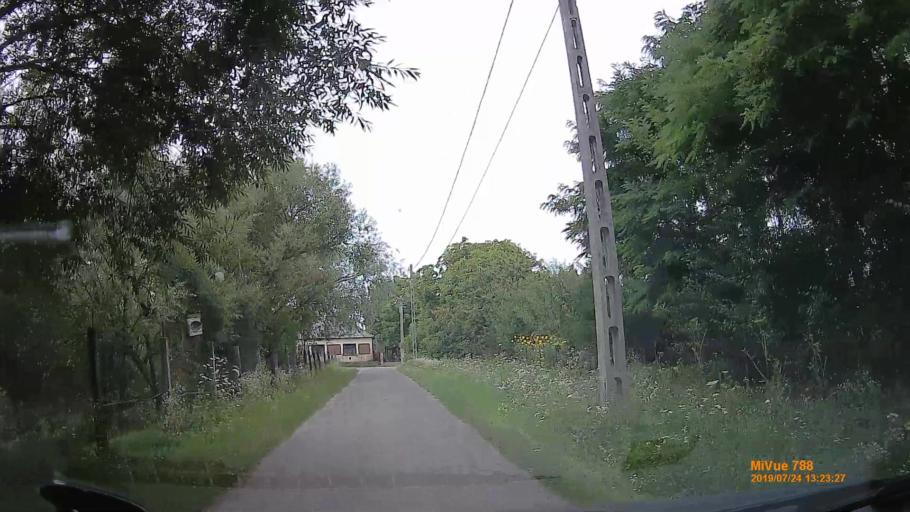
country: UA
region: Zakarpattia
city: Batiovo
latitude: 48.2262
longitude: 22.4199
